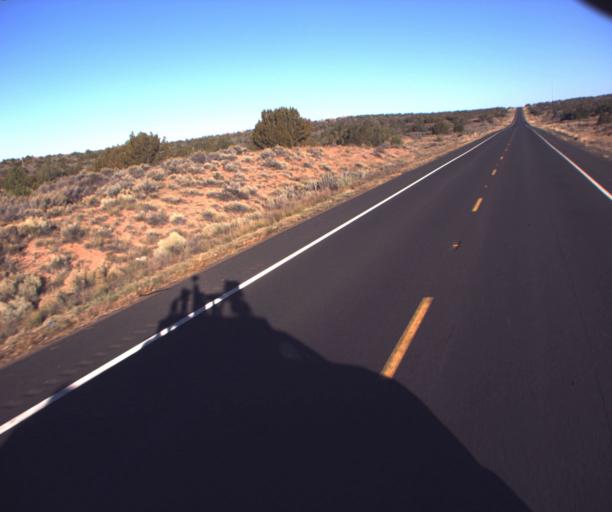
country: US
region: Arizona
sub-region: Apache County
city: Houck
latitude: 35.3349
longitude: -109.4430
